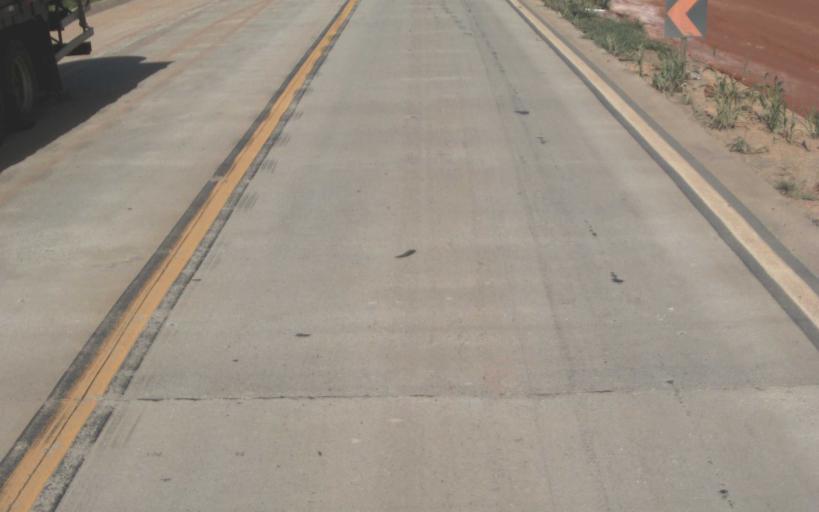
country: BR
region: Minas Gerais
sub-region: Barao De Cocais
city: Barao de Cocais
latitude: -19.7586
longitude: -43.4687
